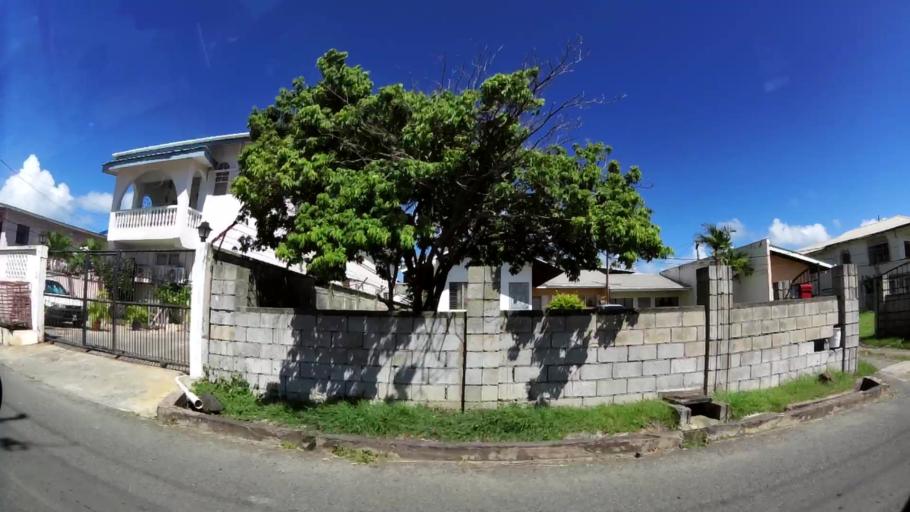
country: TT
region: Tobago
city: Scarborough
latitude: 11.1565
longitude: -60.7746
